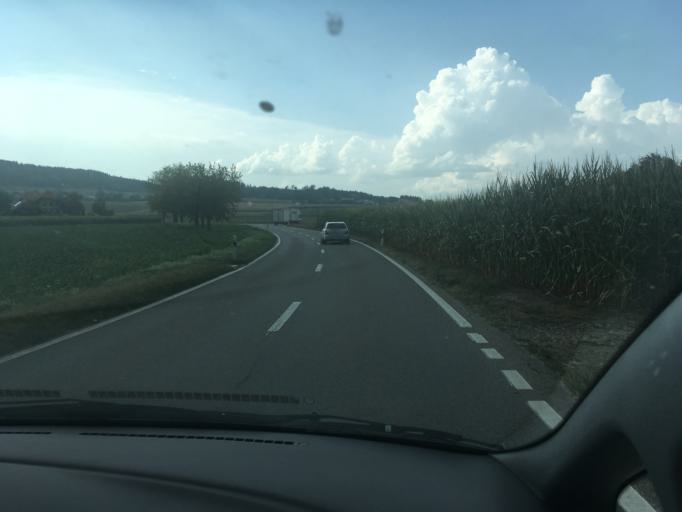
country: CH
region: Bern
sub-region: Seeland District
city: Schupfen
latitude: 47.0066
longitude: 7.3823
